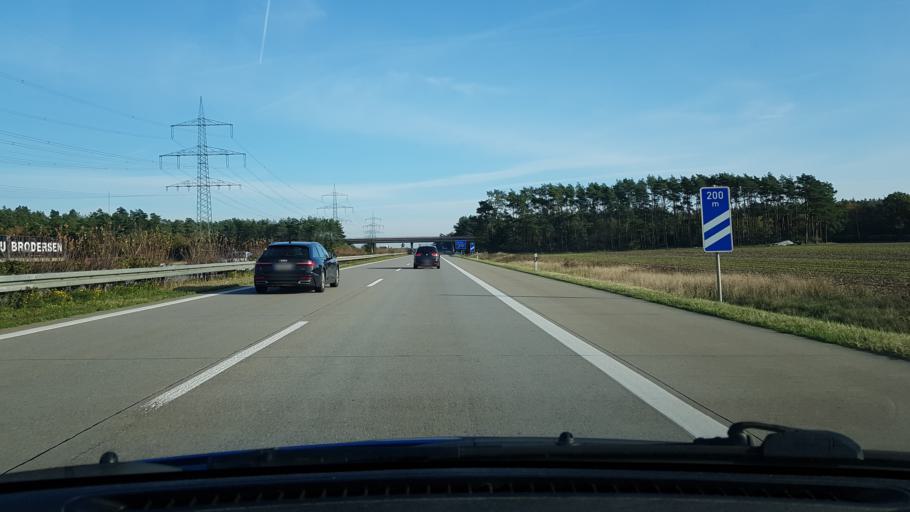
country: DE
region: Mecklenburg-Vorpommern
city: Zarrentin
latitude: 53.5113
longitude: 10.8895
